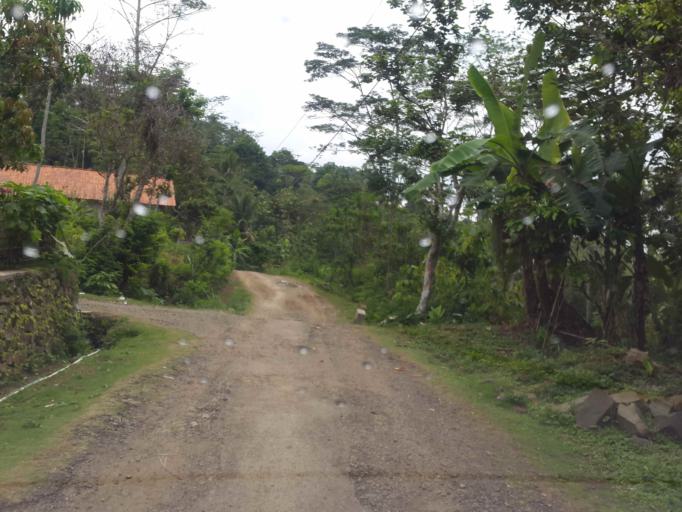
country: ID
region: Central Java
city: Bantarmangu
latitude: -7.3451
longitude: 108.9561
